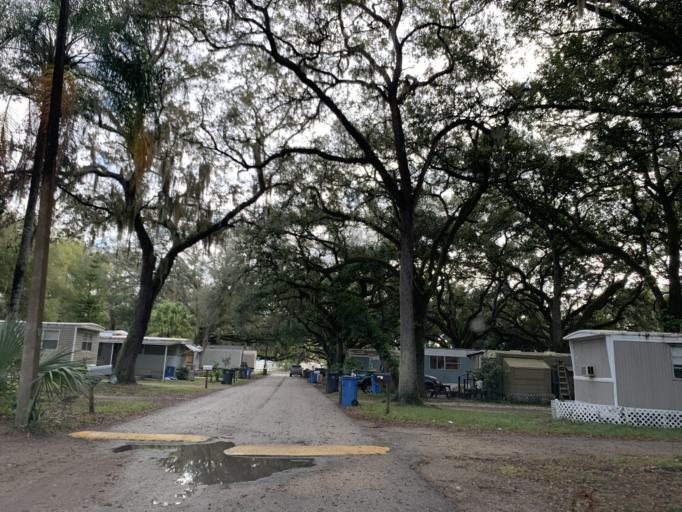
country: US
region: Florida
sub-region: Hillsborough County
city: Mango
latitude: 27.9857
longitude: -82.3199
